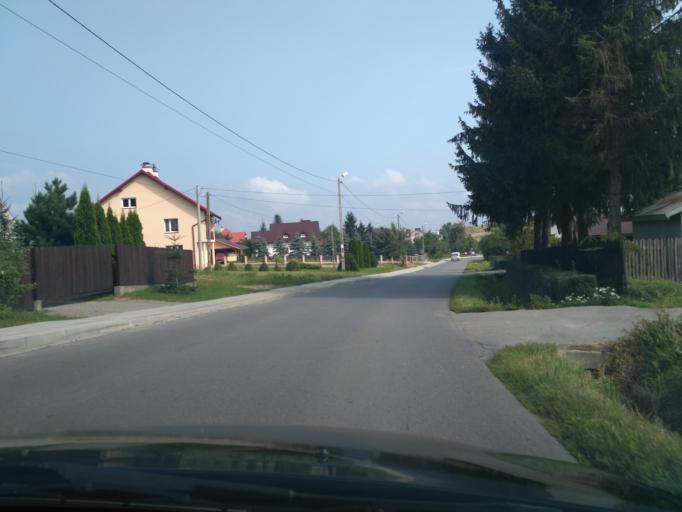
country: PL
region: Subcarpathian Voivodeship
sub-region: Powiat strzyzowski
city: Czudec
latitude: 49.9746
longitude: 21.8365
